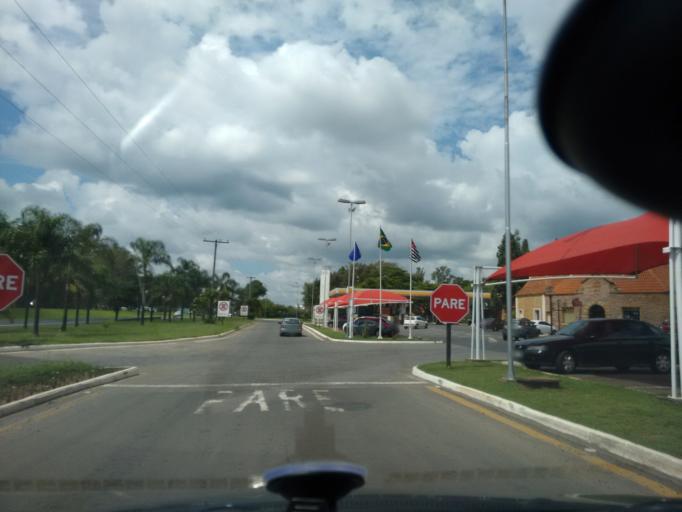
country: BR
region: Sao Paulo
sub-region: Sao Carlos
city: Sao Carlos
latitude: -22.0928
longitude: -47.8316
